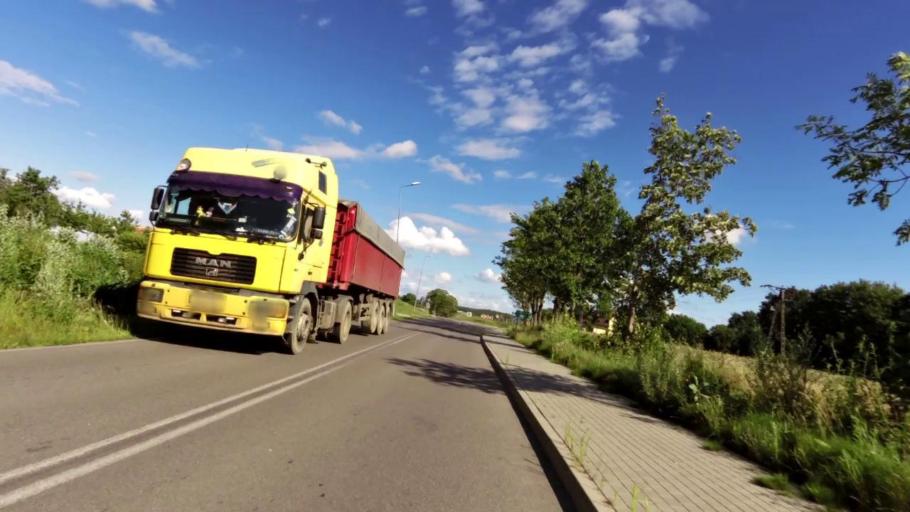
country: PL
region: West Pomeranian Voivodeship
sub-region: Powiat slawienski
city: Slawno
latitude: 54.4553
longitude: 16.7401
